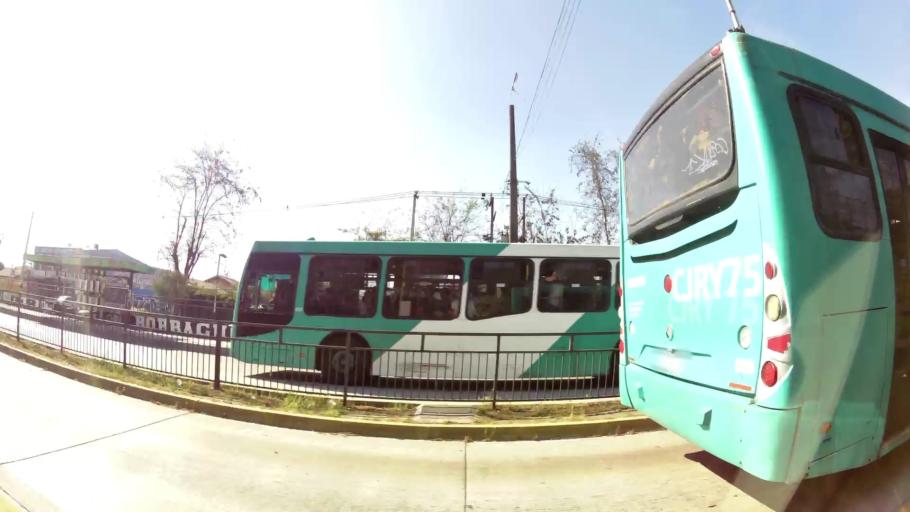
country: CL
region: Santiago Metropolitan
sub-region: Provincia de Santiago
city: Villa Presidente Frei, Nunoa, Santiago, Chile
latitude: -33.4702
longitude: -70.5720
